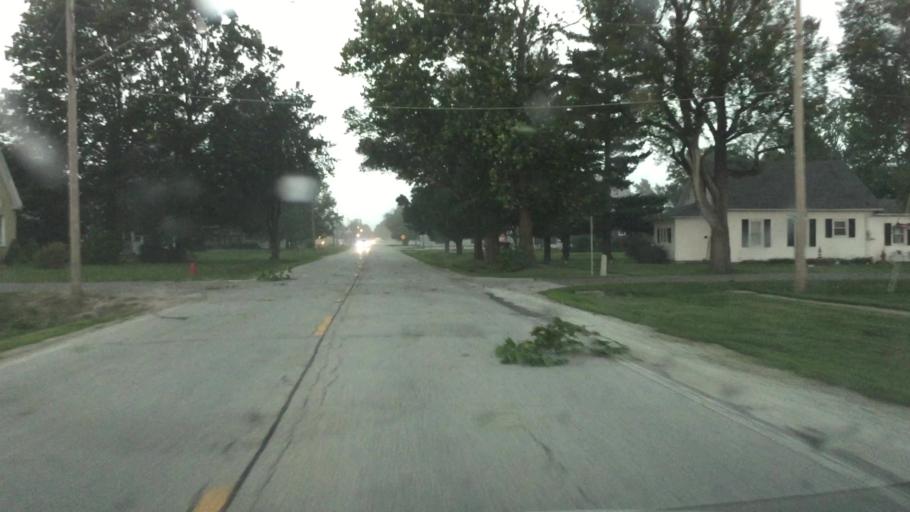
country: US
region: Illinois
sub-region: Adams County
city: Camp Point
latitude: 40.2315
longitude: -91.0577
